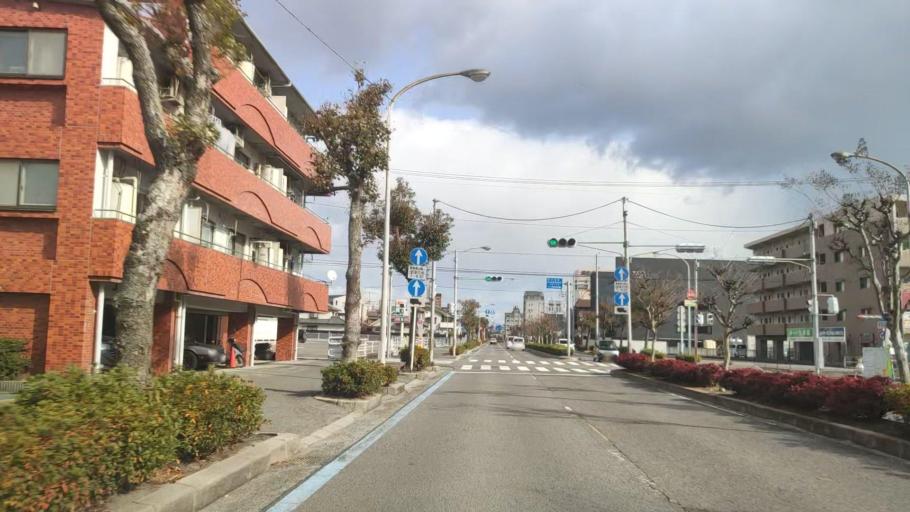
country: JP
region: Ehime
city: Hojo
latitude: 34.0624
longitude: 132.9863
